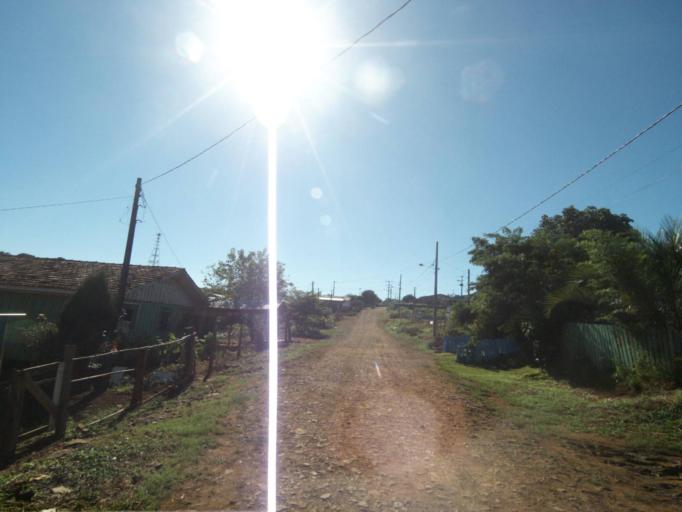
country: BR
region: Parana
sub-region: Pinhao
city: Pinhao
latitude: -25.8399
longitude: -52.0326
